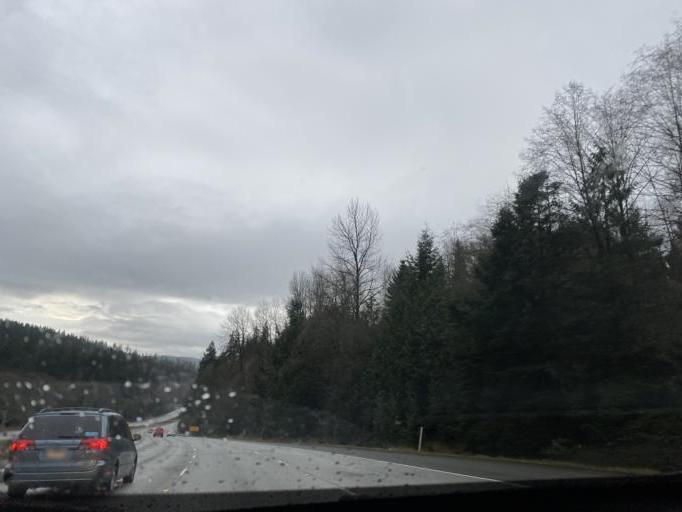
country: US
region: Washington
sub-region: King County
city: Fall City
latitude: 47.5218
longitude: -121.9347
